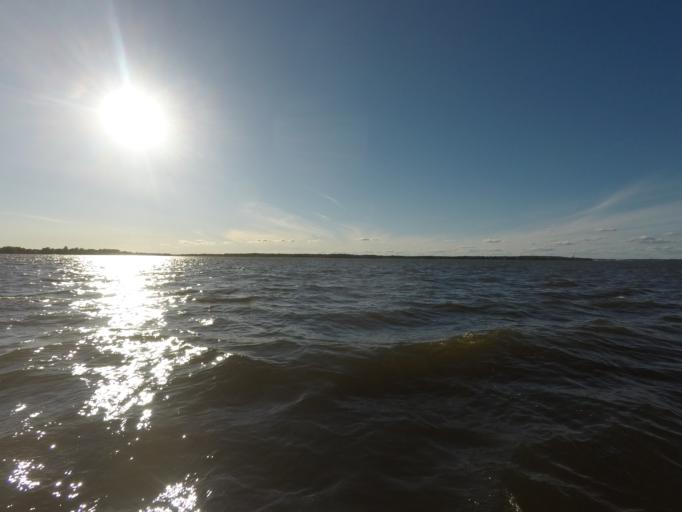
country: SE
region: Vaestmanland
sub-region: Vasteras
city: Vasteras
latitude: 59.5191
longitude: 16.5876
